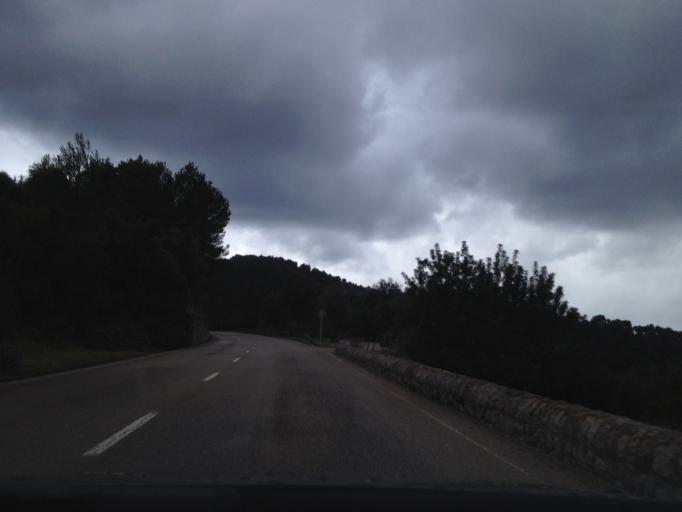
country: ES
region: Balearic Islands
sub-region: Illes Balears
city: Soller
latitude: 39.7741
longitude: 2.7001
